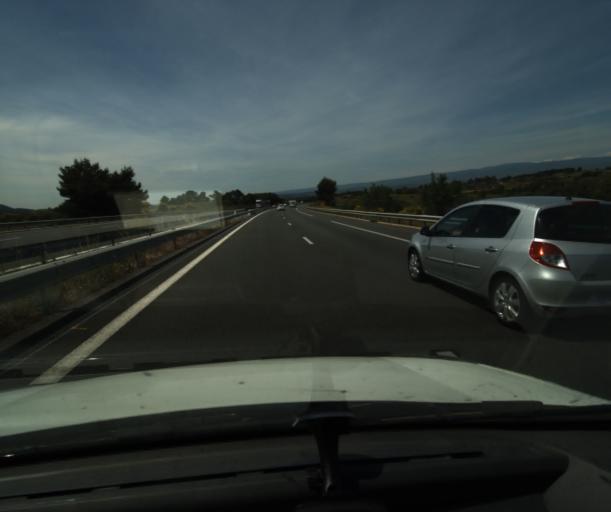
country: FR
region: Languedoc-Roussillon
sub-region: Departement de l'Aude
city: Capendu
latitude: 43.1722
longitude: 2.6038
